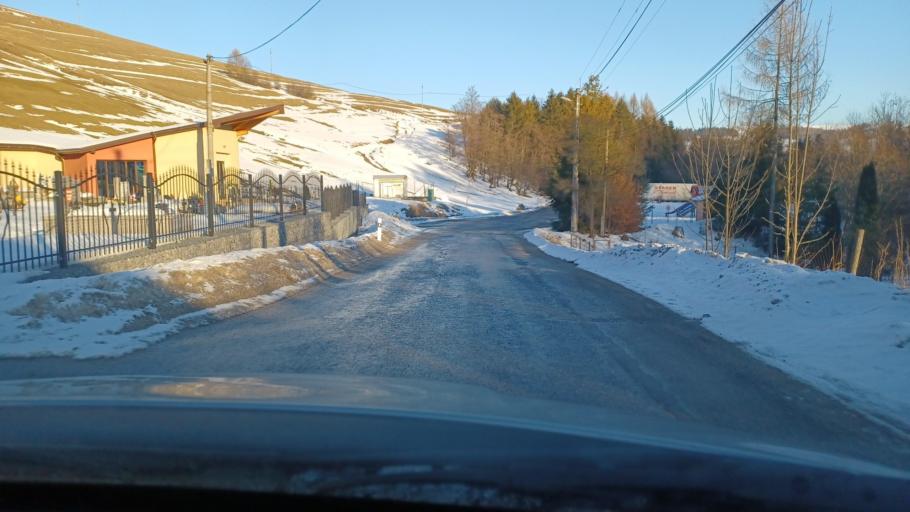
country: SK
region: Zilinsky
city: Tvrdosin
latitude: 49.3643
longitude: 19.5328
